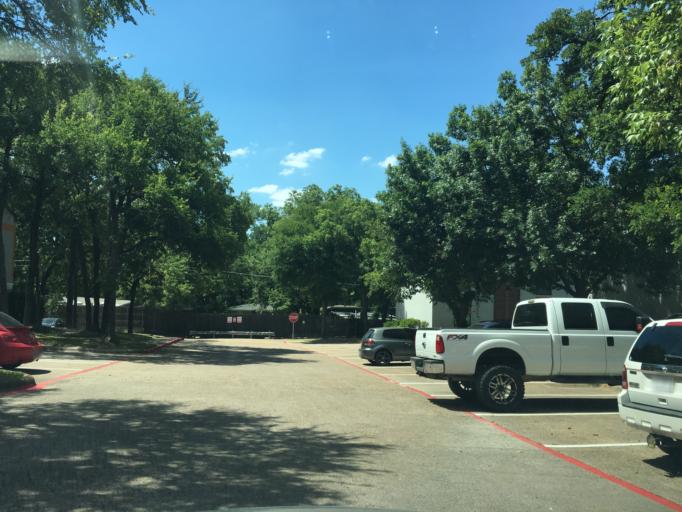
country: US
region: Texas
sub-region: Dallas County
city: Garland
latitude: 32.8438
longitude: -96.6946
